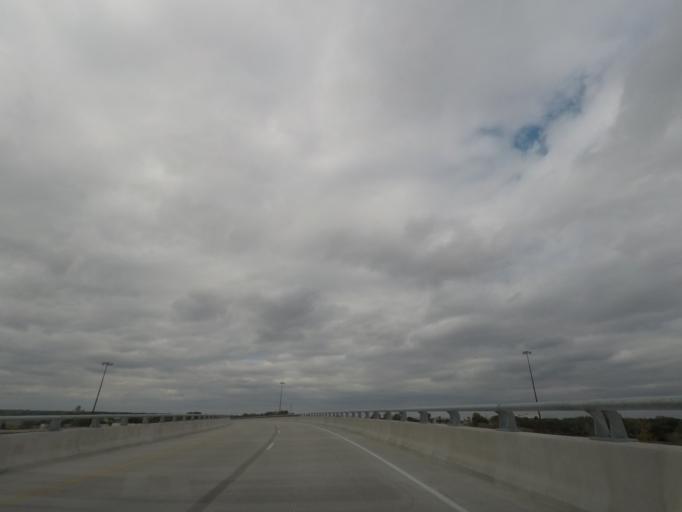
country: US
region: Iowa
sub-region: Story County
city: Ames
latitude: 42.0059
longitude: -93.5703
